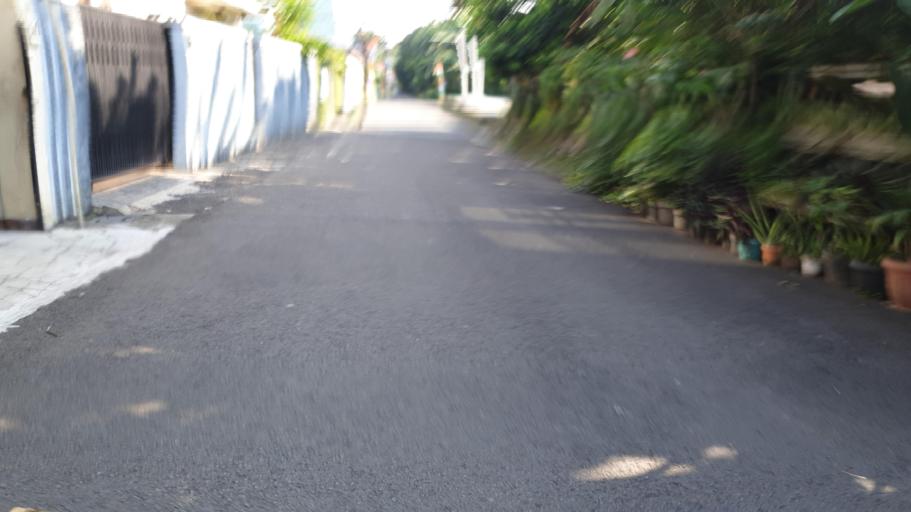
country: ID
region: Jakarta Raya
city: Jakarta
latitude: -6.2988
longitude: 106.8384
